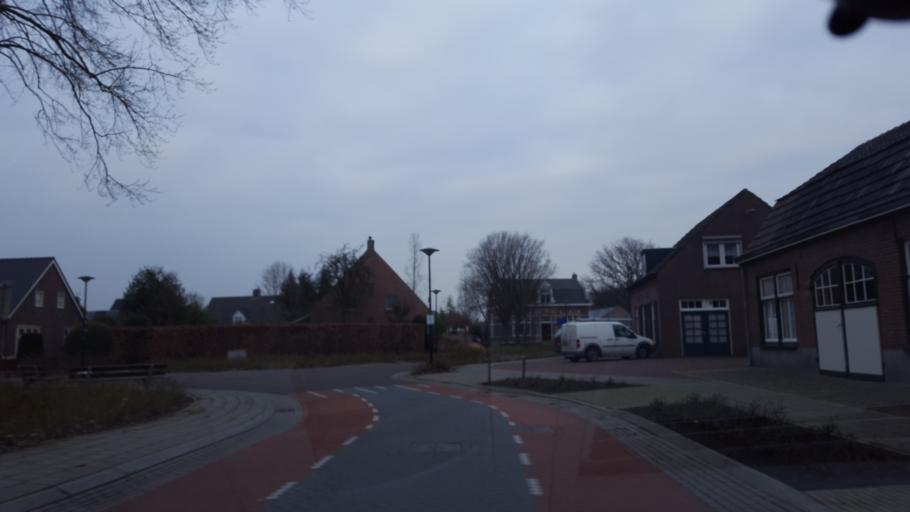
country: NL
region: North Brabant
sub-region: Gemeente Asten
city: Asten
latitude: 51.4434
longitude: 5.7608
